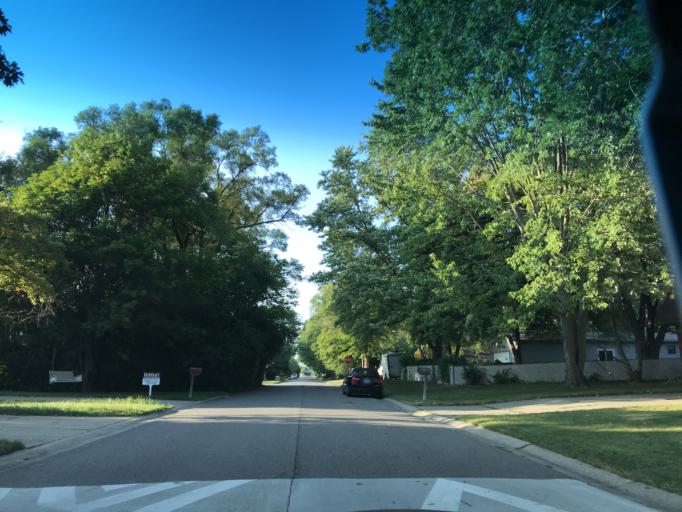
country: US
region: Michigan
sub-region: Washtenaw County
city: Ypsilanti
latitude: 42.2487
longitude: -83.6677
